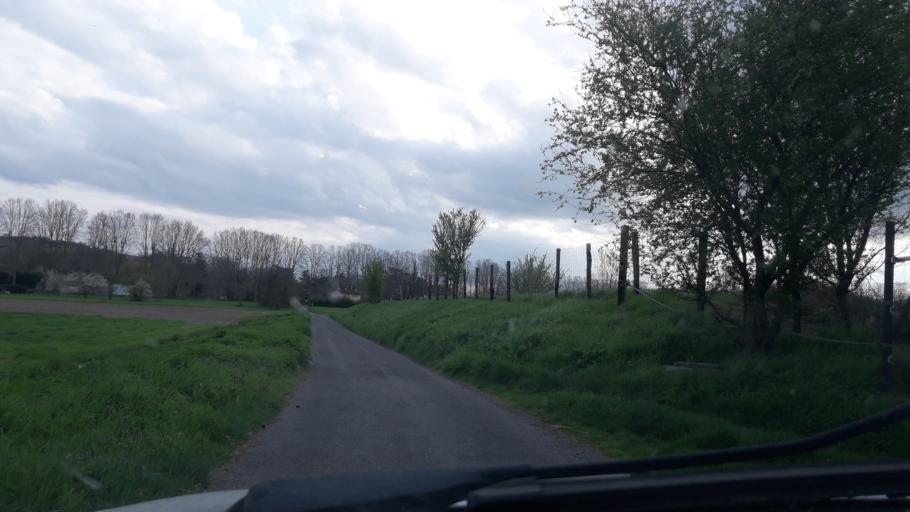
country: FR
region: Midi-Pyrenees
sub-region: Departement de la Haute-Garonne
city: Carbonne
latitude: 43.2949
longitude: 1.2203
